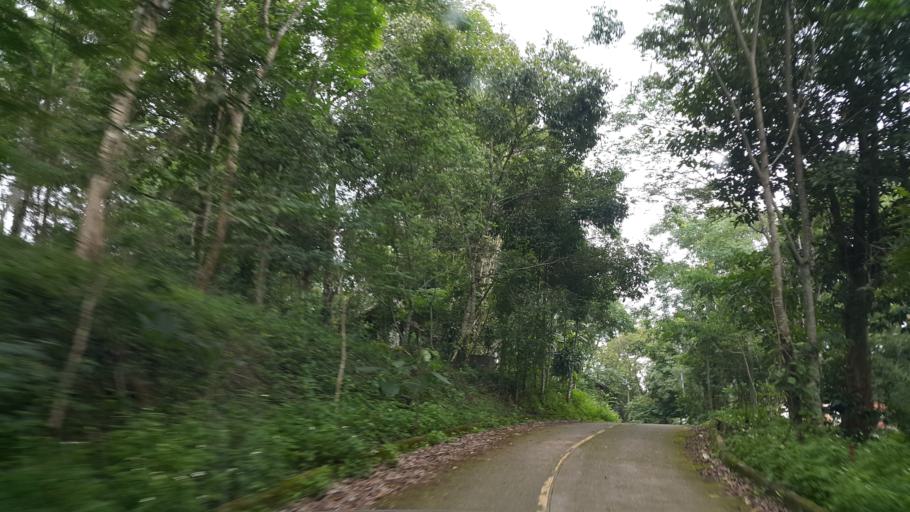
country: TH
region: Lampang
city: Mueang Pan
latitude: 18.8306
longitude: 99.3833
